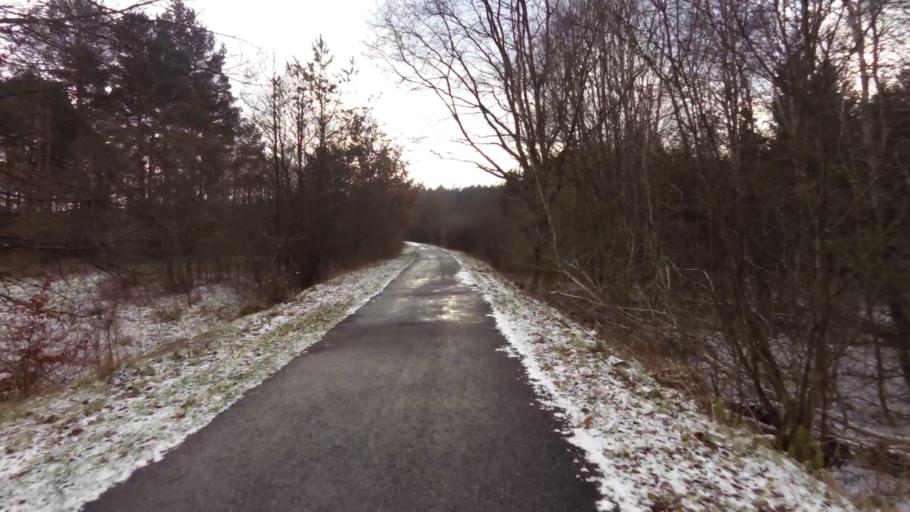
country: PL
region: West Pomeranian Voivodeship
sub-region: Powiat drawski
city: Zlocieniec
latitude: 53.5816
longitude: 16.0413
